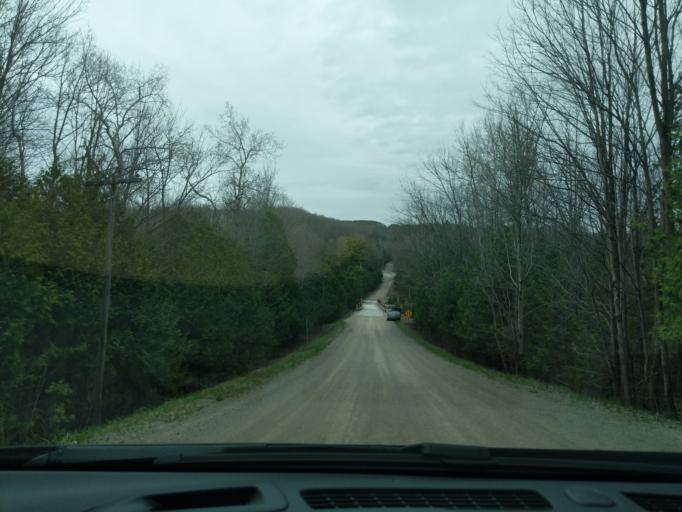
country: CA
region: Ontario
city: Orangeville
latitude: 43.9980
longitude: -80.0153
